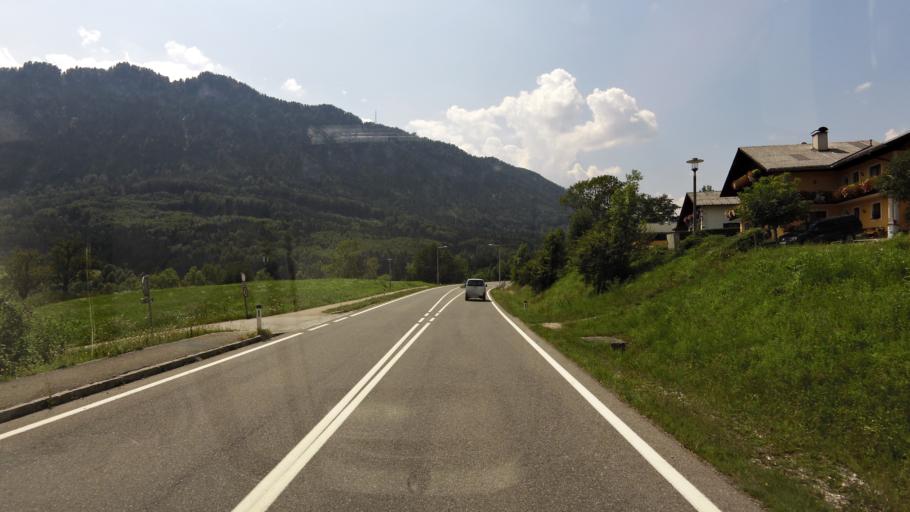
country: AT
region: Upper Austria
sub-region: Politischer Bezirk Vocklabruck
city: Steinbach am Attersee
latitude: 47.8046
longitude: 13.4813
